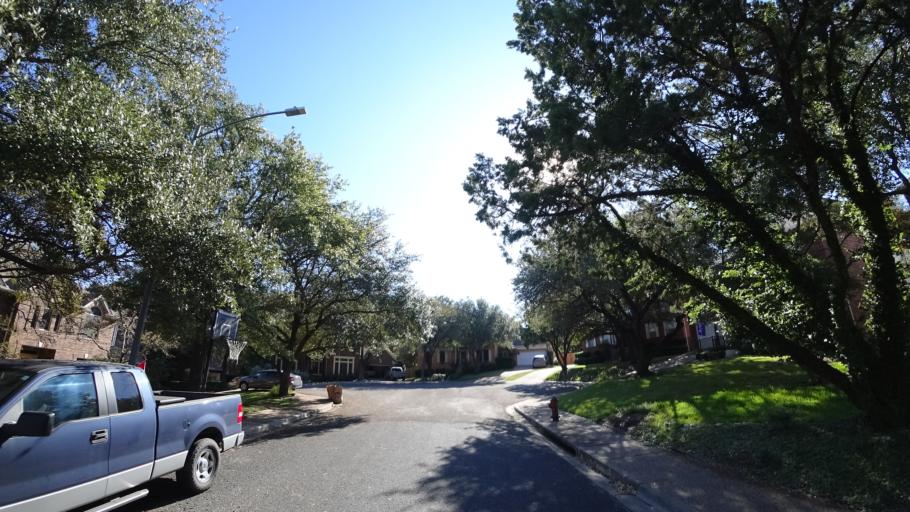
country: US
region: Texas
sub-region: Williamson County
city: Jollyville
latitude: 30.4112
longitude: -97.7619
